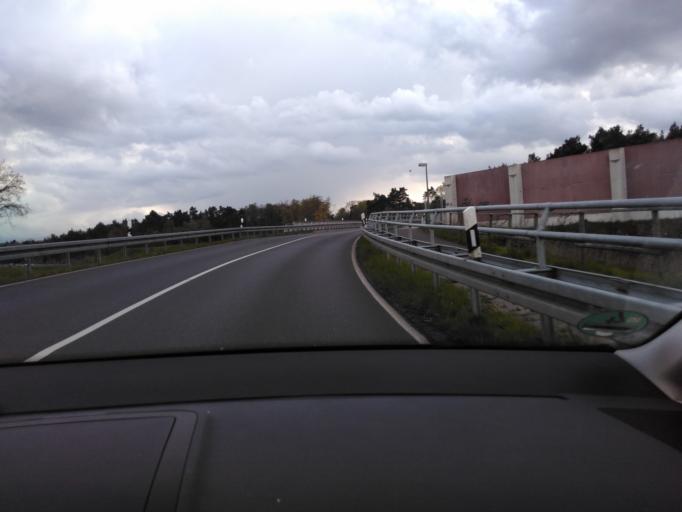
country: DE
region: North Rhine-Westphalia
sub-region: Regierungsbezirk Detmold
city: Bielefeld
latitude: 51.9609
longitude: 8.5023
